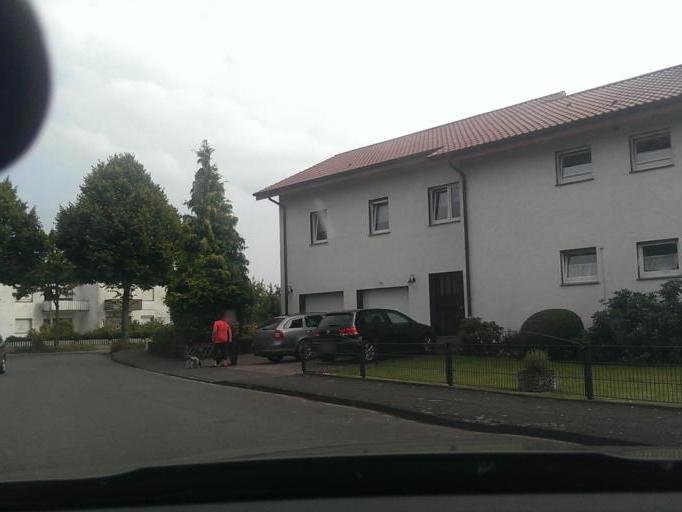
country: DE
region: North Rhine-Westphalia
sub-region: Regierungsbezirk Detmold
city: Delbruck
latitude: 51.7690
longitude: 8.5511
